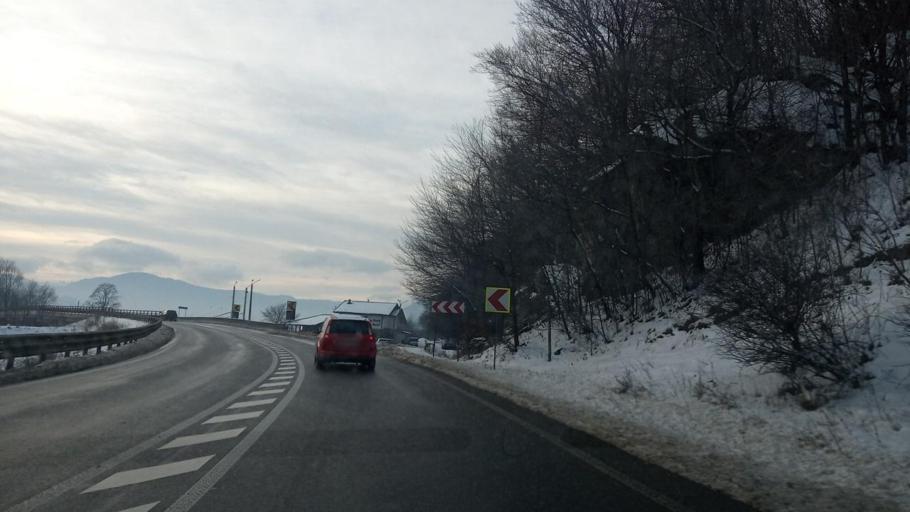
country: RO
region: Suceava
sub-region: Comuna Frasin
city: Bucsoaia
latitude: 47.5452
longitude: 25.8485
